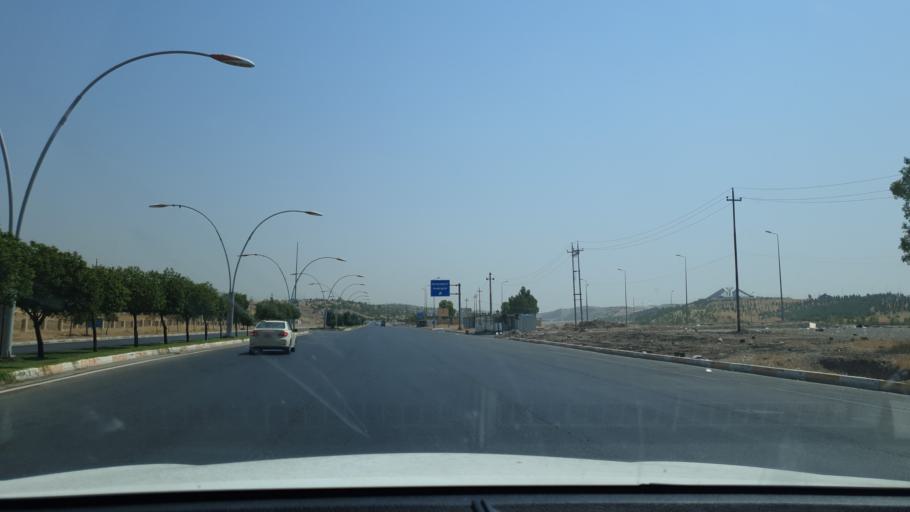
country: IQ
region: Arbil
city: Erbil
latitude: 36.2127
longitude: 44.1571
